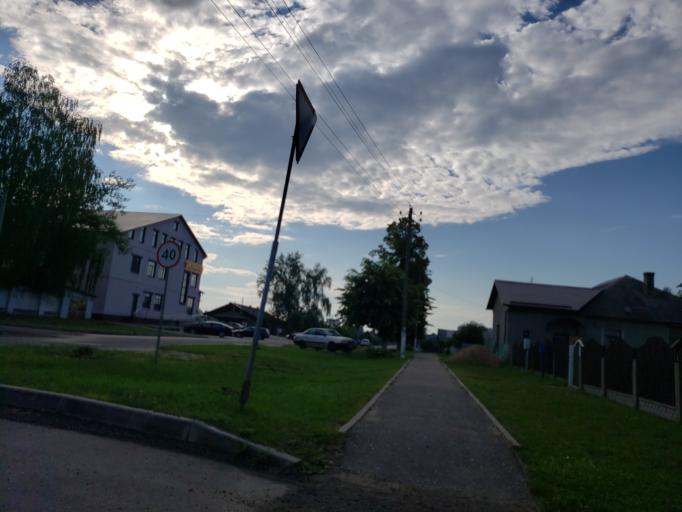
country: BY
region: Minsk
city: Chervyen'
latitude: 53.7055
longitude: 28.4358
